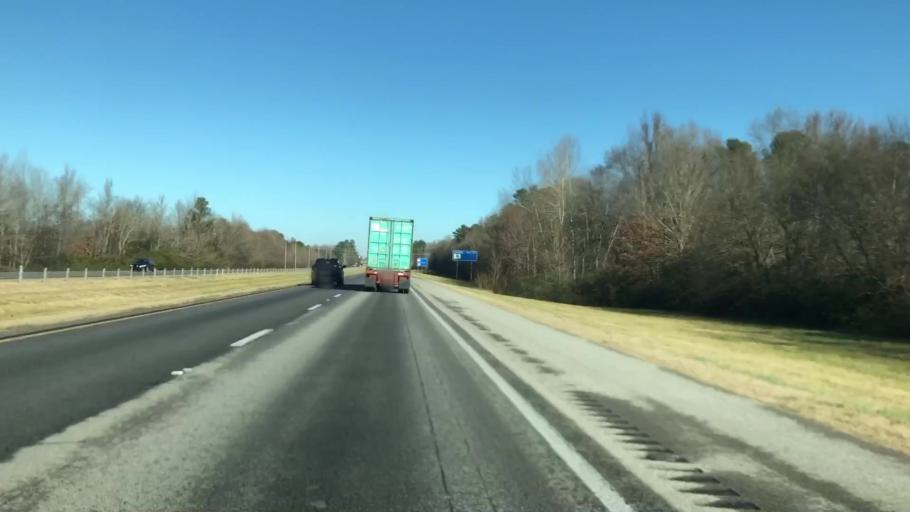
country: US
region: Alabama
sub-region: Limestone County
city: Athens
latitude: 34.8175
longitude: -86.9387
